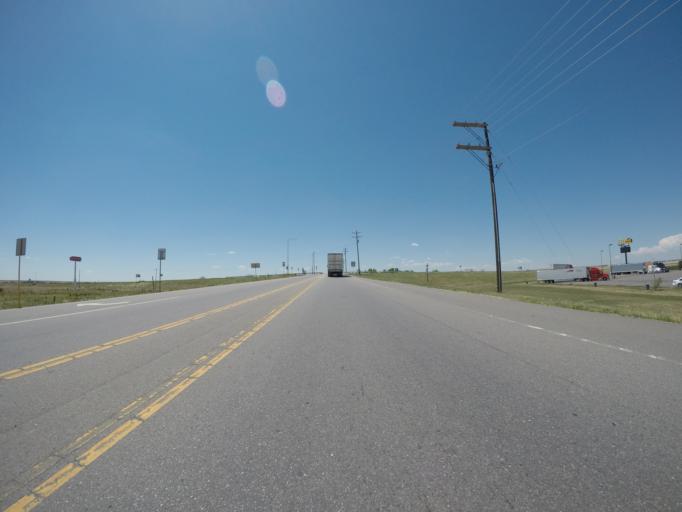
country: US
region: Colorado
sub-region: Adams County
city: Bennett
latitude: 39.7399
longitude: -104.4334
